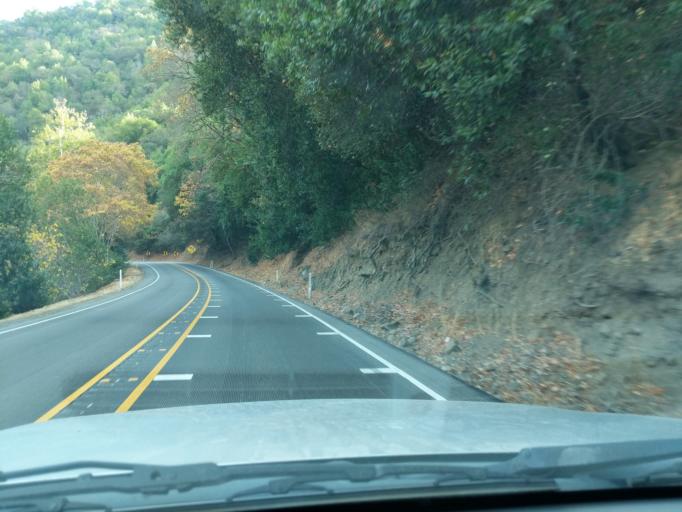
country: US
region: California
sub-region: Alameda County
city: Fremont
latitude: 37.5920
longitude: -121.9371
